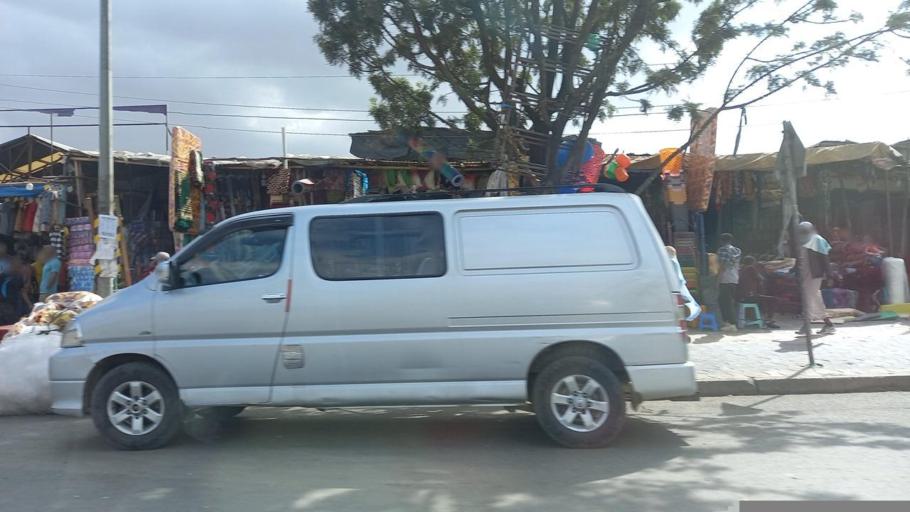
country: ET
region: Adis Abeba
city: Addis Ababa
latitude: 9.0206
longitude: 38.8618
